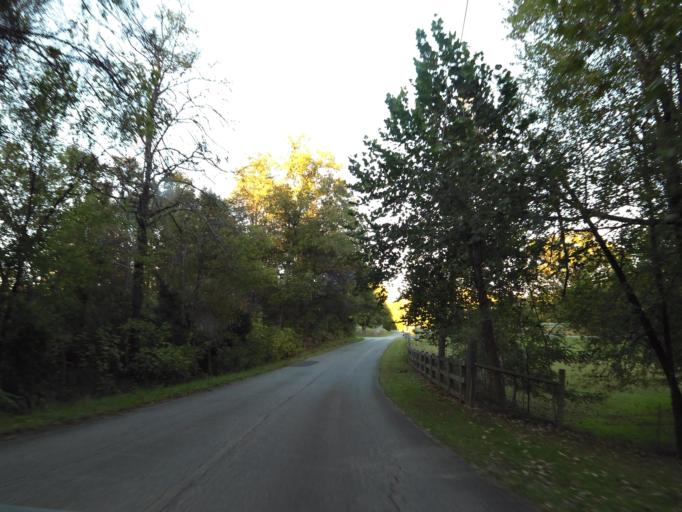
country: US
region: Tennessee
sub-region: Sevier County
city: Seymour
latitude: 35.8092
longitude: -83.7564
